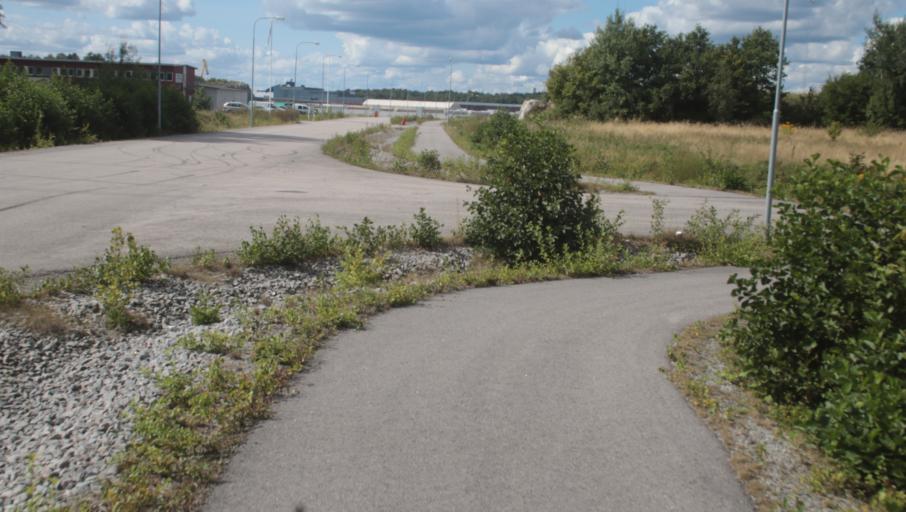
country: SE
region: Blekinge
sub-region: Karlshamns Kommun
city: Karlshamn
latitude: 56.1623
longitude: 14.8375
